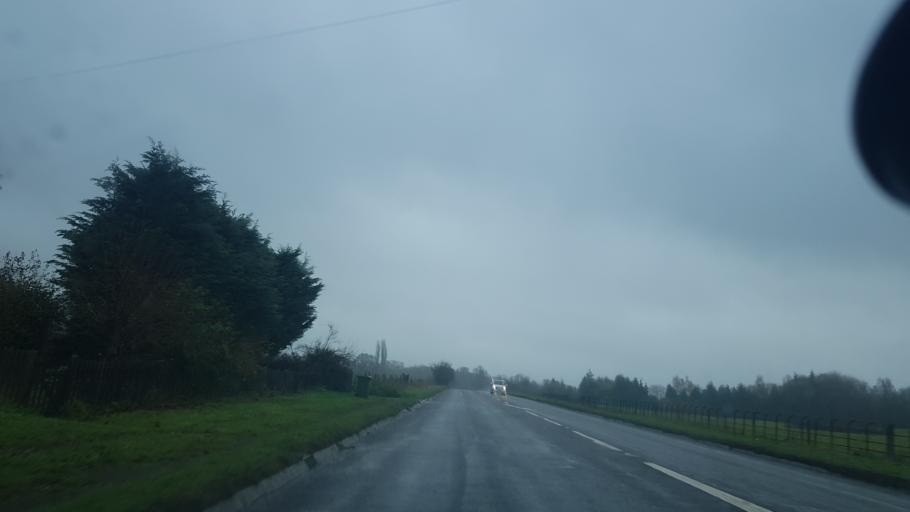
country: GB
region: England
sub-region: Surrey
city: Chilworth
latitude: 51.2244
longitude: -0.4789
